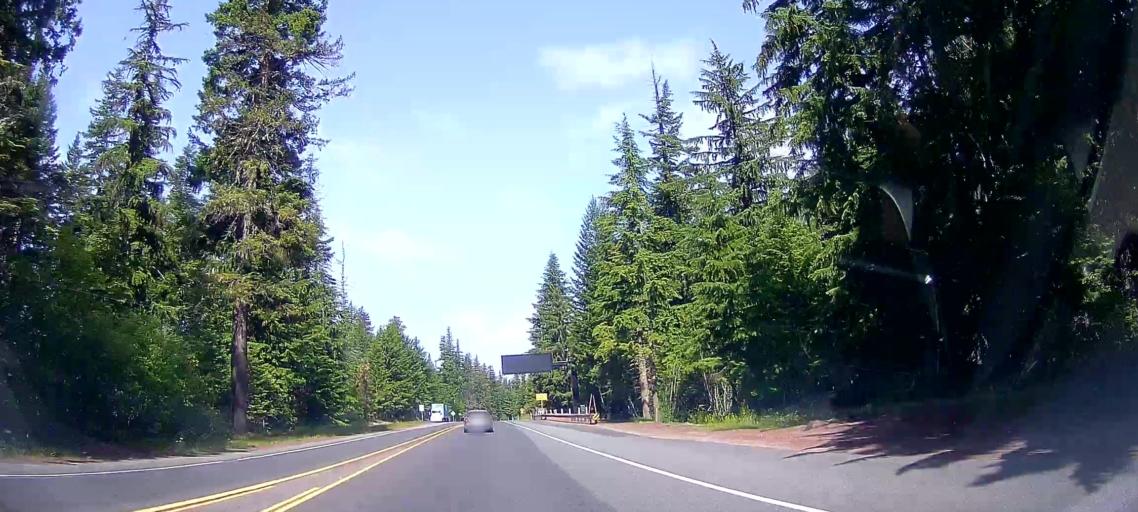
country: US
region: Oregon
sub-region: Clackamas County
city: Mount Hood Village
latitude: 45.1319
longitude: -121.6045
